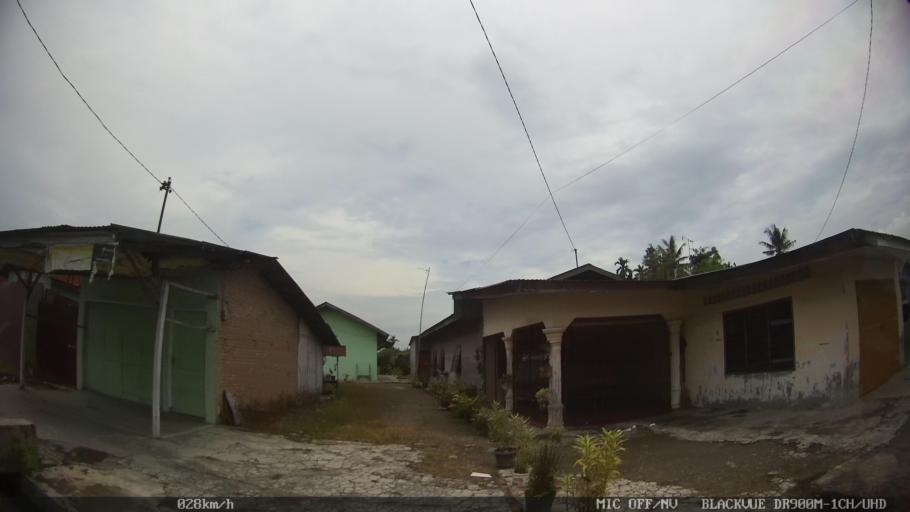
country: ID
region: North Sumatra
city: Binjai
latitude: 3.6228
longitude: 98.5551
